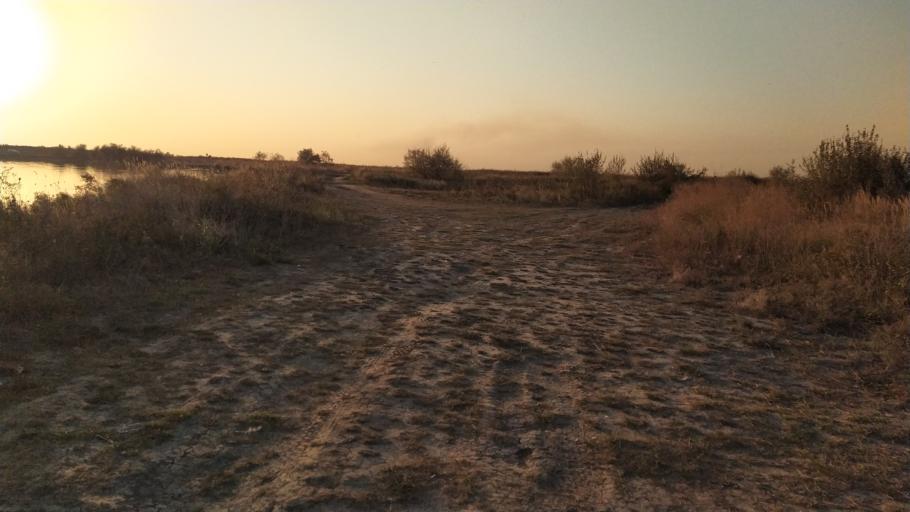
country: RU
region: Rostov
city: Bataysk
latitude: 47.1437
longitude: 39.6482
